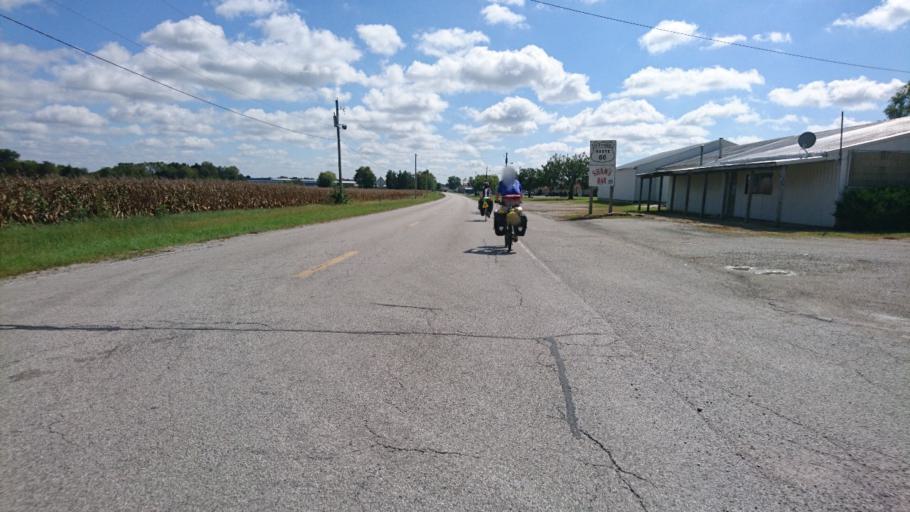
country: US
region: Illinois
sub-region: Montgomery County
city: Litchfield
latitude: 39.1688
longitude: -89.6668
